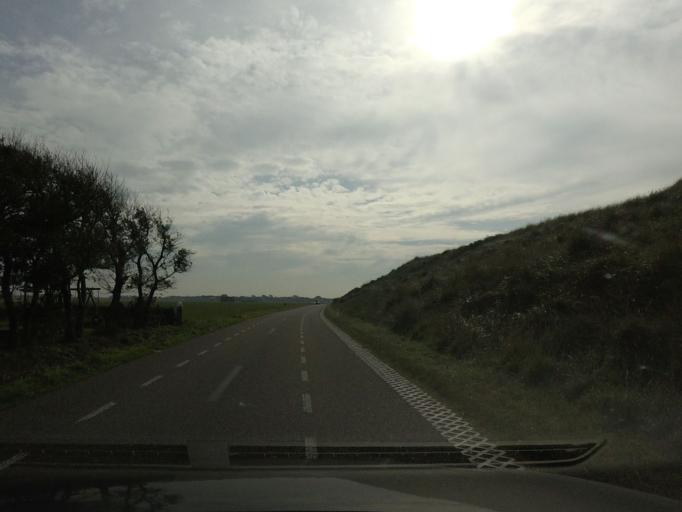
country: NL
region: North Holland
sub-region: Gemeente Den Helder
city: Den Helder
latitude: 52.8726
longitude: 4.7145
